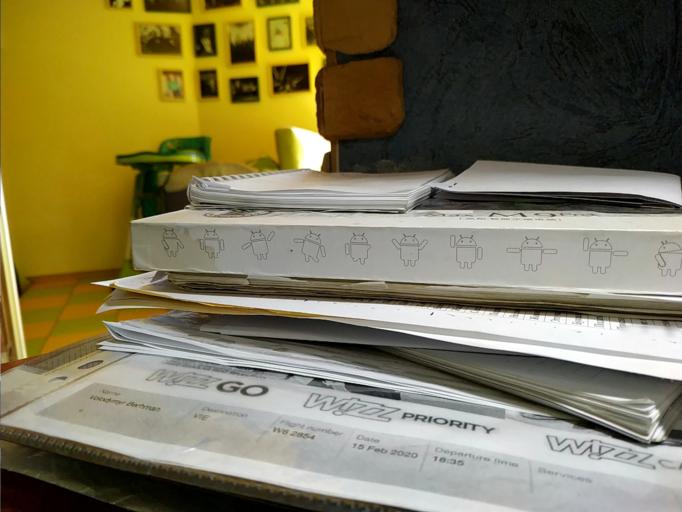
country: RU
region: Pskov
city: Plyussa
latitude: 58.6644
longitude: 29.3251
